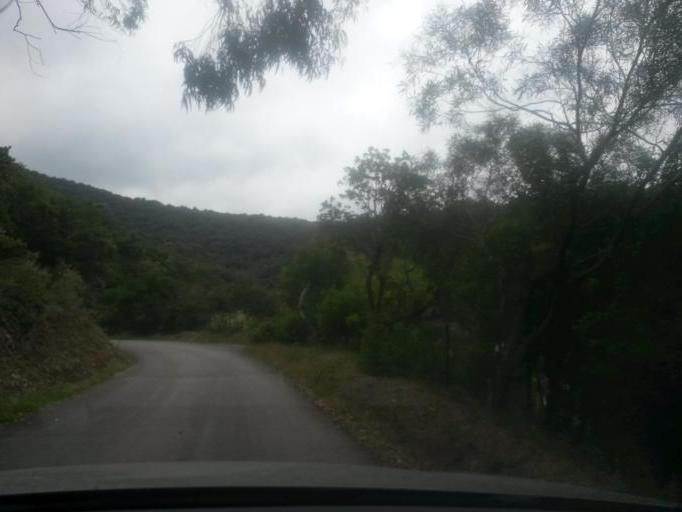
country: IT
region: Tuscany
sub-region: Provincia di Livorno
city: Porto Azzurro
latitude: 42.7440
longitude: 10.4067
